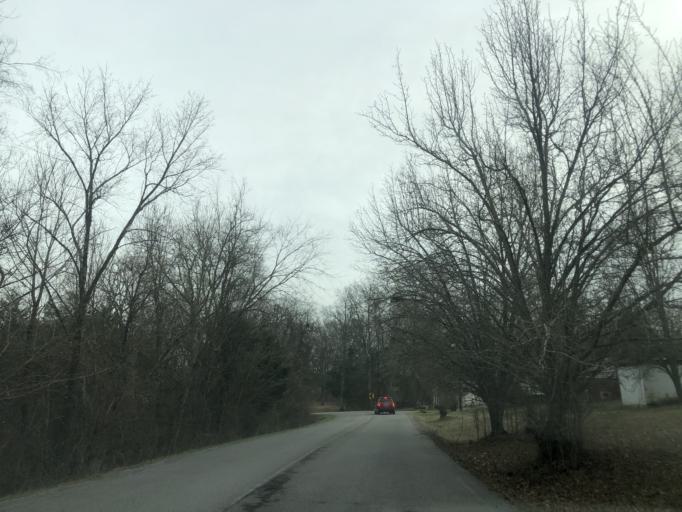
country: US
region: Tennessee
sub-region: Wilson County
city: Lebanon
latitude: 36.2545
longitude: -86.2676
